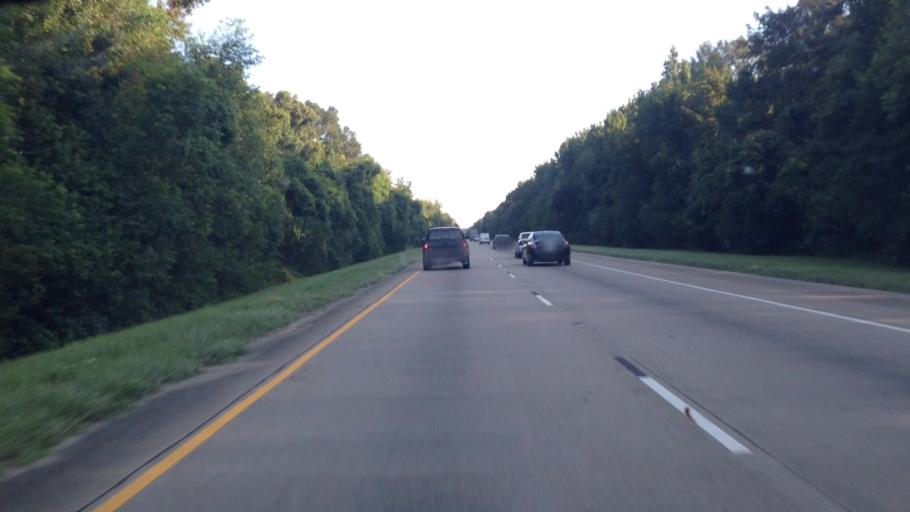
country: US
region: Louisiana
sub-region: Ascension Parish
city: Prairieville
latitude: 30.2878
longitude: -90.9899
